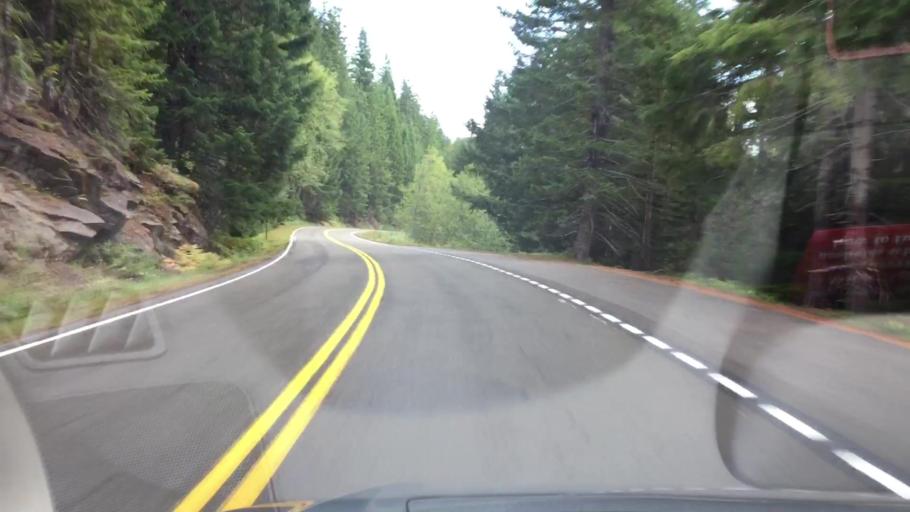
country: US
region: Washington
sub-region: Pierce County
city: Buckley
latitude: 46.7640
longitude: -121.6319
